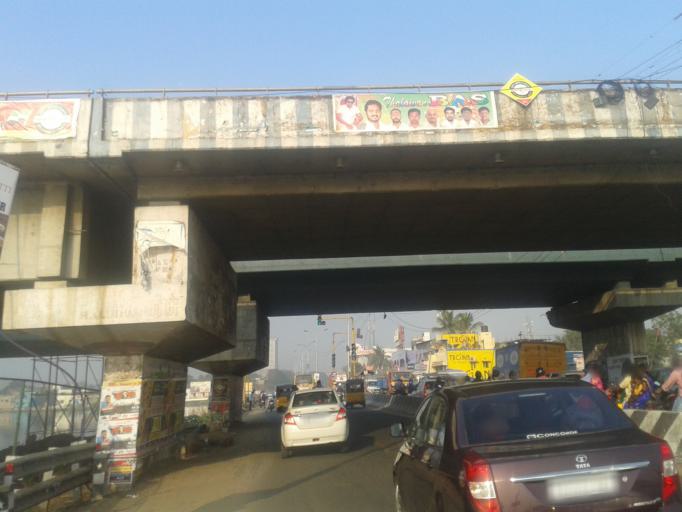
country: IN
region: Tamil Nadu
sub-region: Thiruvallur
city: Porur
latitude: 13.0361
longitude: 80.1494
